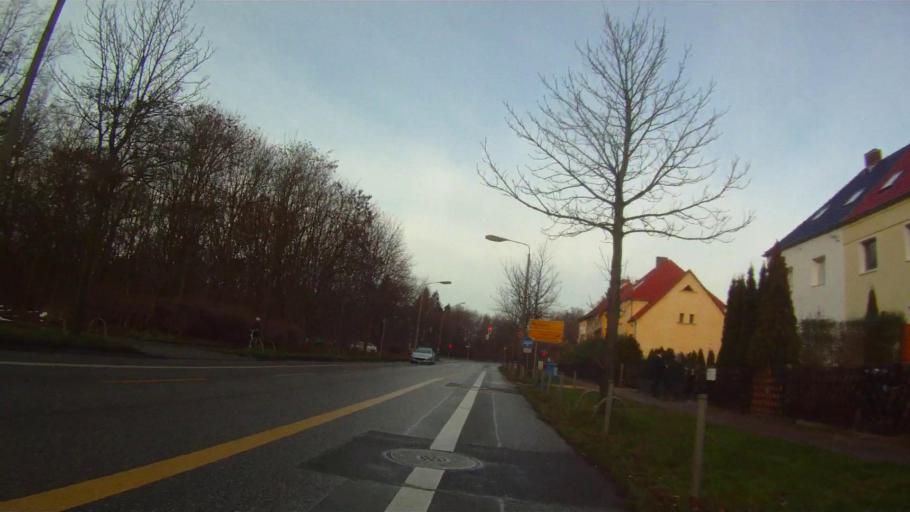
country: DE
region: Berlin
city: Johannisthal
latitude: 52.4574
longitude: 13.4991
